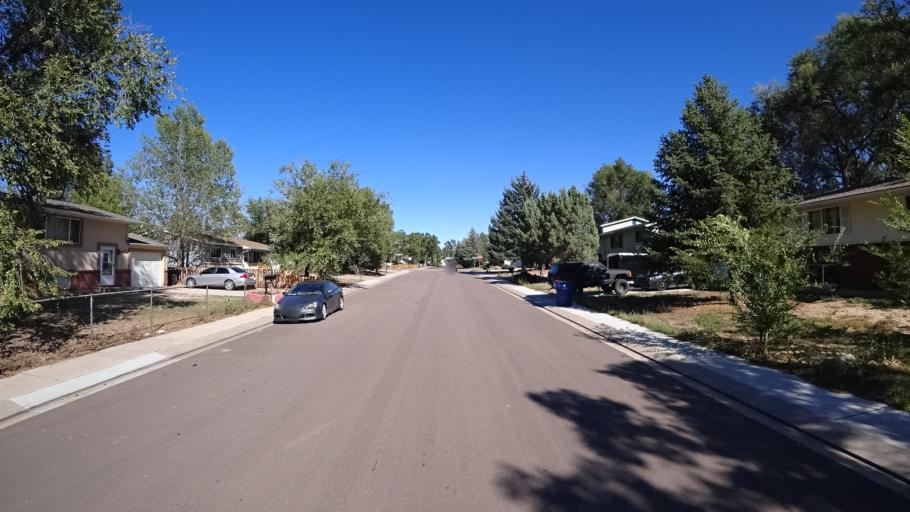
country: US
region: Colorado
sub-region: El Paso County
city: Stratmoor
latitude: 38.8002
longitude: -104.7441
